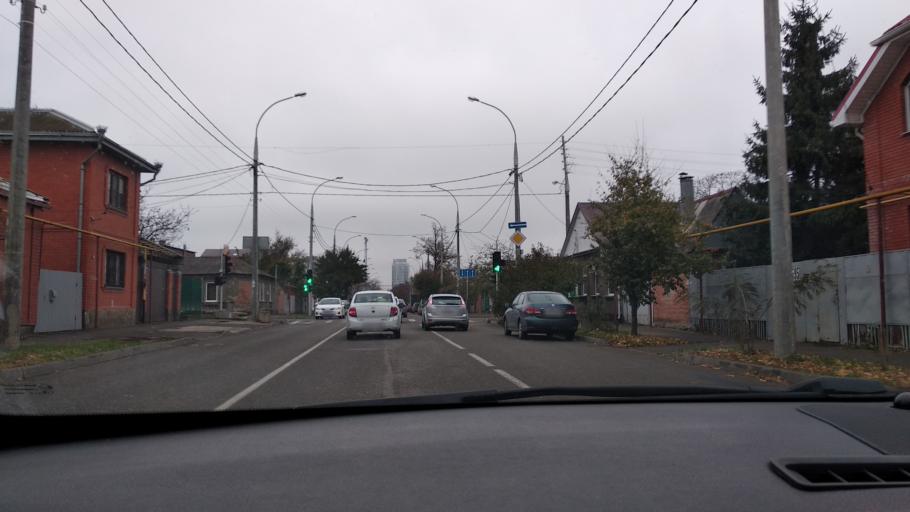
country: RU
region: Krasnodarskiy
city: Krasnodar
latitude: 45.0338
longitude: 38.9877
